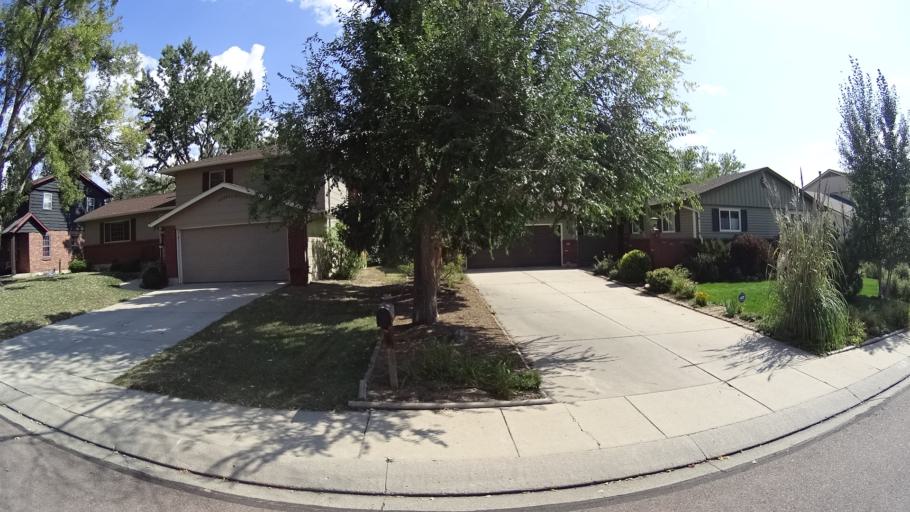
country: US
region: Colorado
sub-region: El Paso County
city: Cimarron Hills
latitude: 38.8715
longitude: -104.7521
